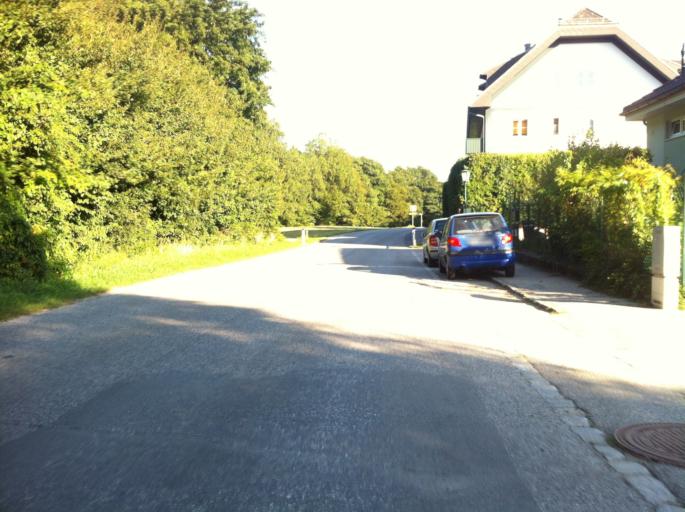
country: AT
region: Lower Austria
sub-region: Politischer Bezirk Wien-Umgebung
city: Pressbaum
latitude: 48.2025
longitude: 16.1072
